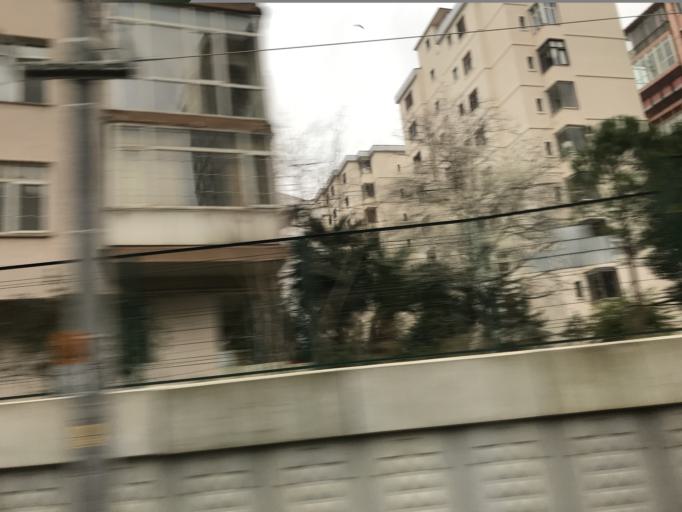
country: TR
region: Istanbul
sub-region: Atasehir
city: Atasehir
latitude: 40.9740
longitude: 29.0742
